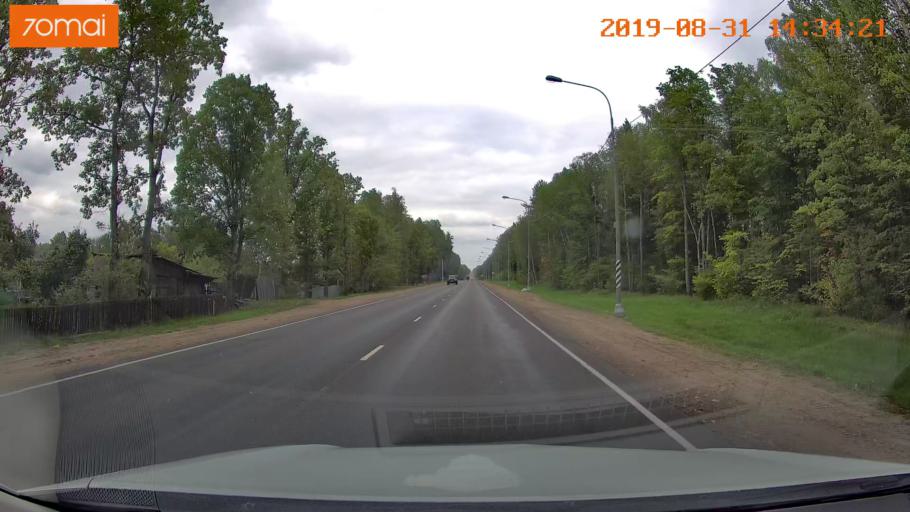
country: RU
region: Smolensk
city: Yekimovichi
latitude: 54.1570
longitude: 33.4361
